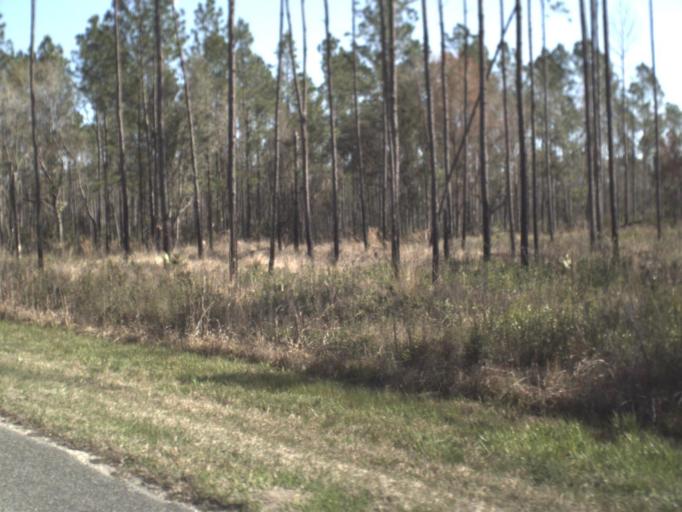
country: US
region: Florida
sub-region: Leon County
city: Woodville
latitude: 30.2643
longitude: -84.0422
